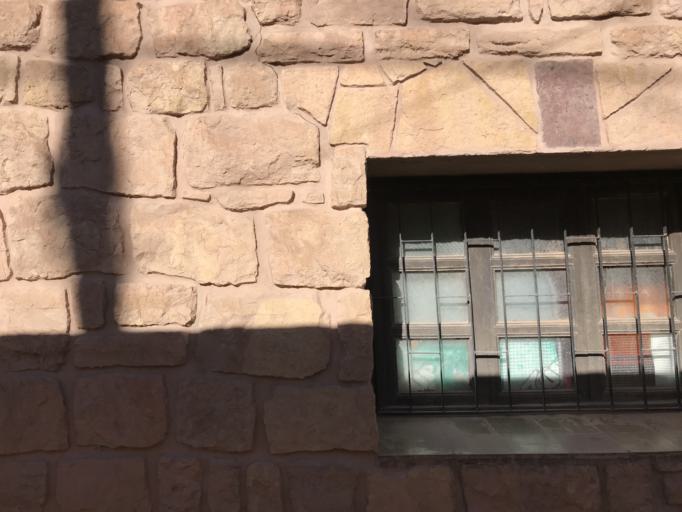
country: AR
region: Jujuy
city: Maimara
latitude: -23.6274
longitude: -65.4092
